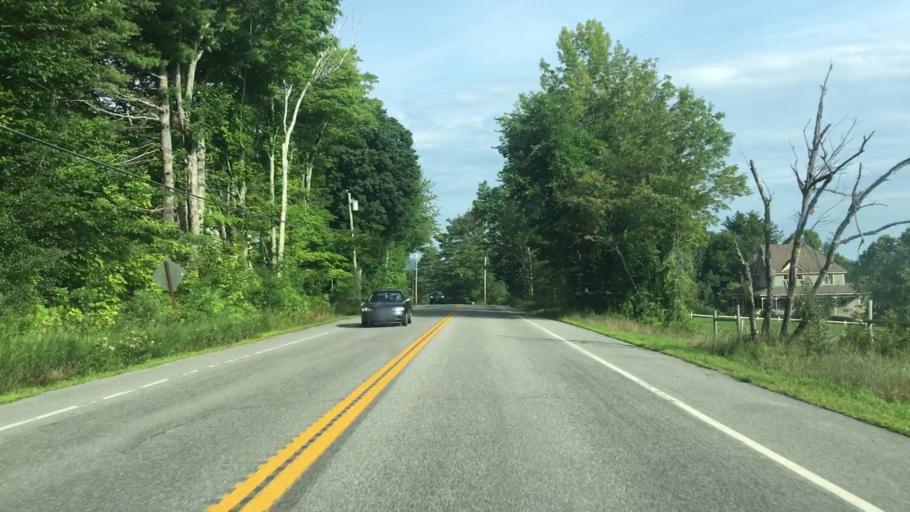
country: US
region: Maine
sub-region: York County
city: Cornish
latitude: 43.7839
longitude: -70.7597
